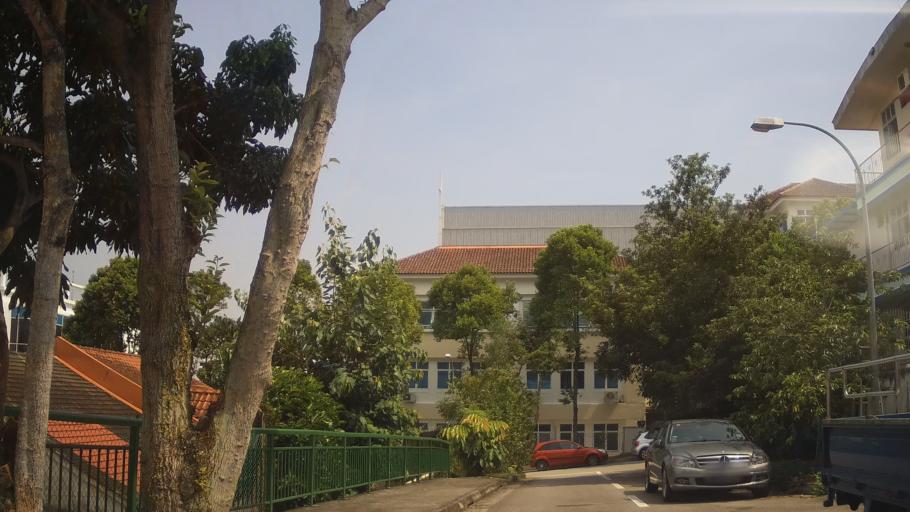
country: MY
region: Johor
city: Johor Bahru
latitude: 1.3609
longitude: 103.7683
